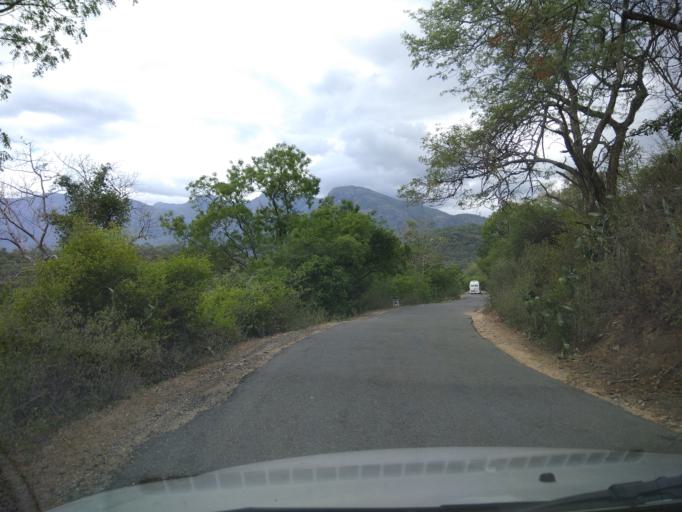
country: IN
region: Tamil Nadu
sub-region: Tiruppur
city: Dhali
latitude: 10.3368
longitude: 77.2179
